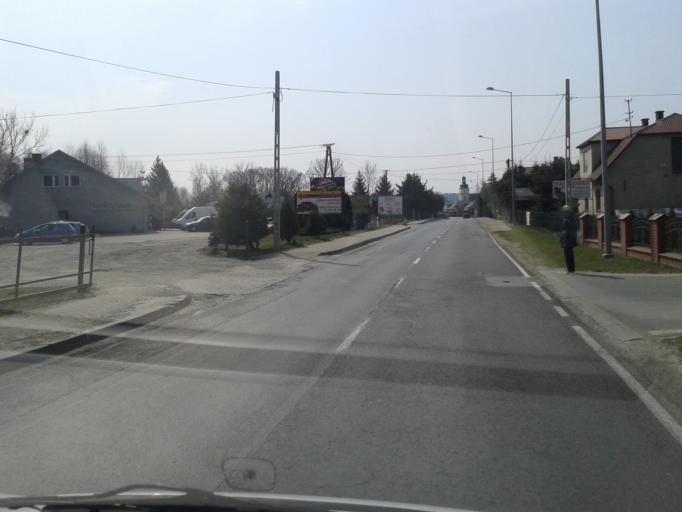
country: PL
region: Subcarpathian Voivodeship
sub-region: Powiat lubaczowski
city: Narol
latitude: 50.3538
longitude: 23.3285
